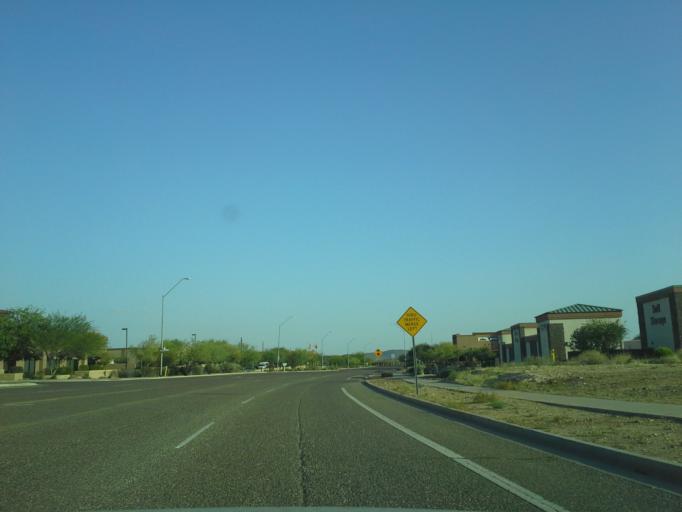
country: US
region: Arizona
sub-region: Maricopa County
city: Anthem
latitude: 33.8674
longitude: -112.1506
